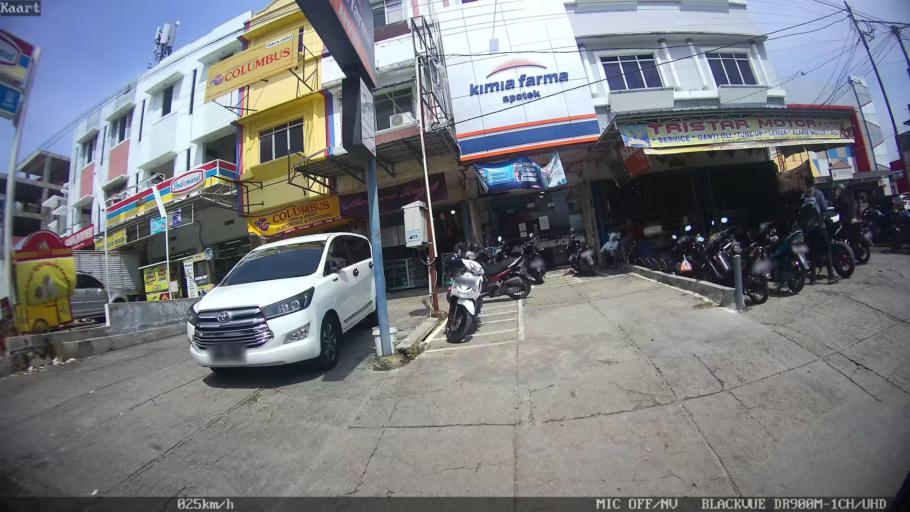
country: ID
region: Lampung
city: Kedaton
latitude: -5.3793
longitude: 105.2721
